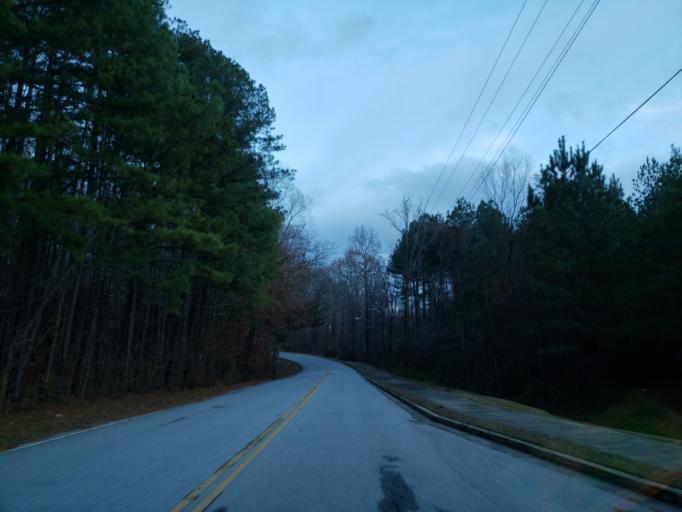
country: US
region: Georgia
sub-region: Fulton County
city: Union City
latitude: 33.6741
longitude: -84.5560
